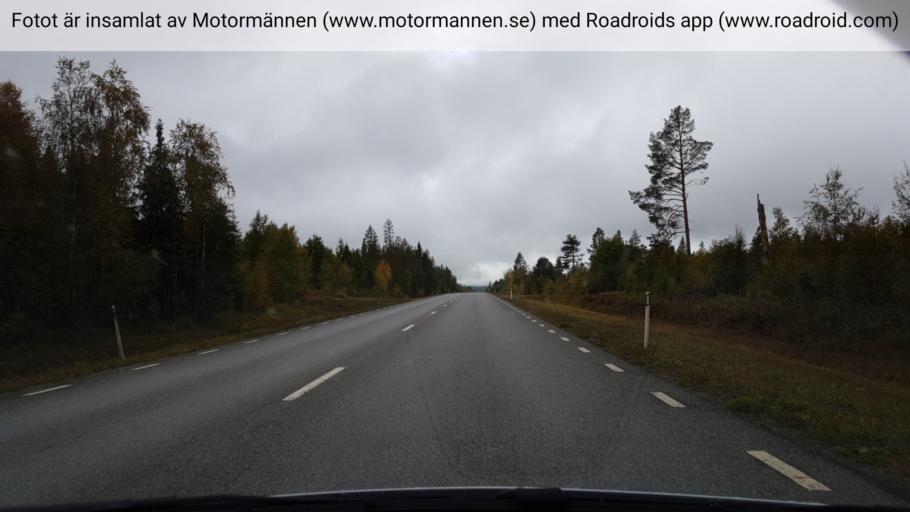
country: SE
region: Jaemtland
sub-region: Stroemsunds Kommun
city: Stroemsund
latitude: 63.7029
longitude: 15.4447
